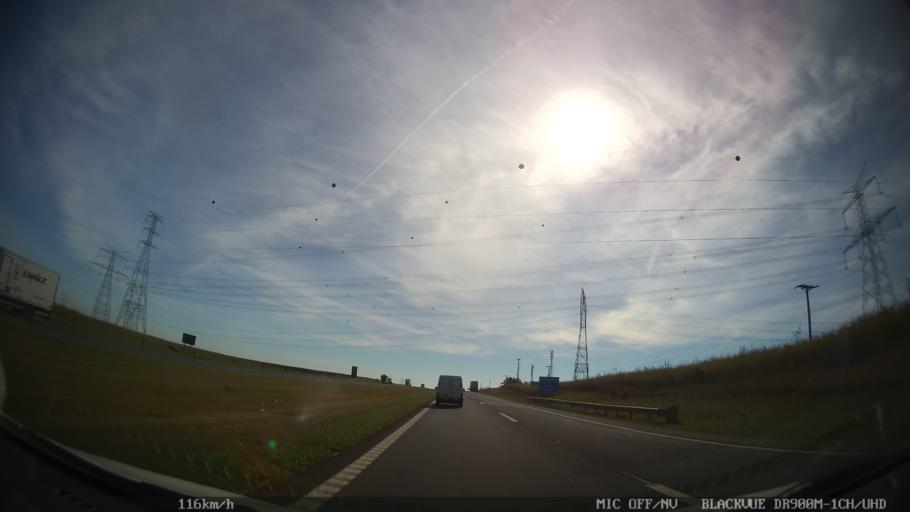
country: BR
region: Sao Paulo
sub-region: Cordeiropolis
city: Cordeiropolis
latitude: -22.4423
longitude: -47.3975
